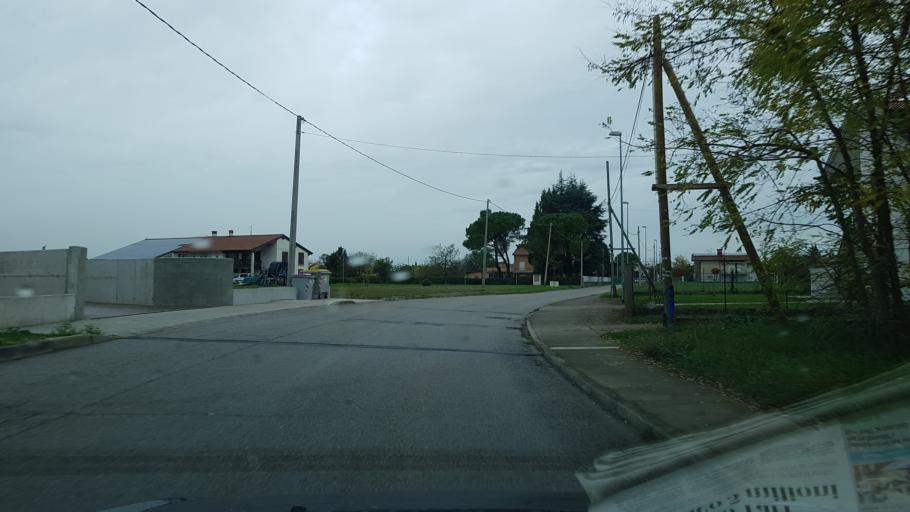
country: IT
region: Friuli Venezia Giulia
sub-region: Provincia di Udine
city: Fiumicello
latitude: 45.8000
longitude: 13.4143
